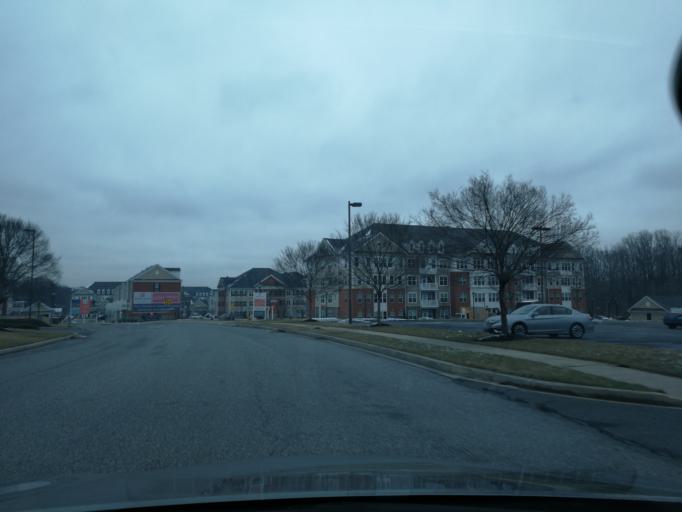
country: US
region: Maryland
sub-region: Harford County
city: Bel Air South
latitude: 39.4656
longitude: -76.3058
